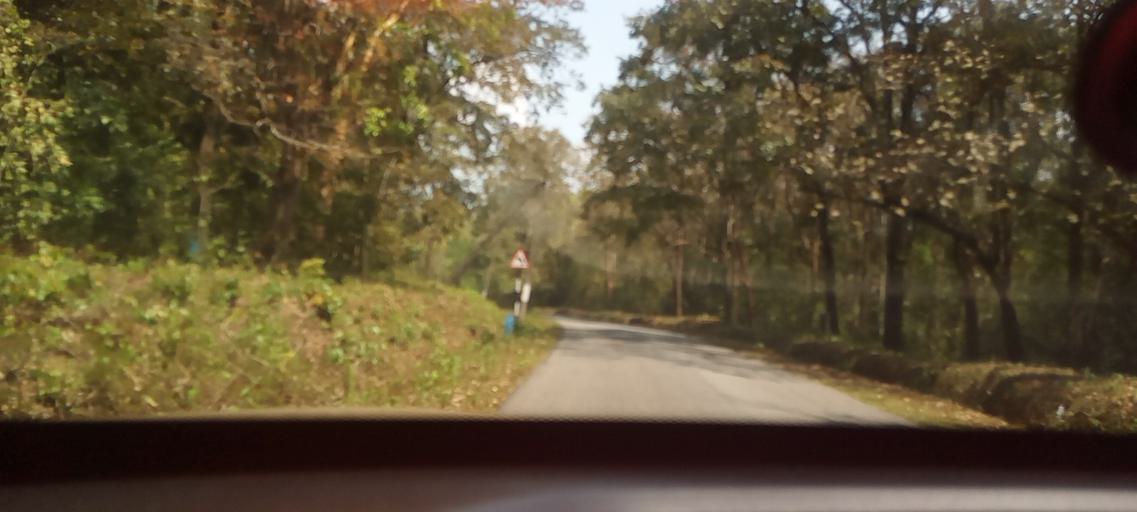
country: IN
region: Karnataka
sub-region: Chikmagalur
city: Koppa
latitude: 13.3524
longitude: 75.4912
